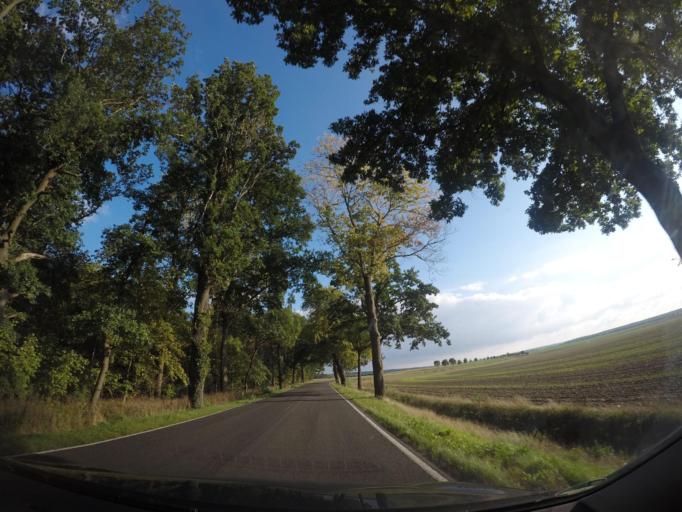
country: DE
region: Saxony-Anhalt
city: Weferlingen
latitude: 52.3418
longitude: 11.0728
